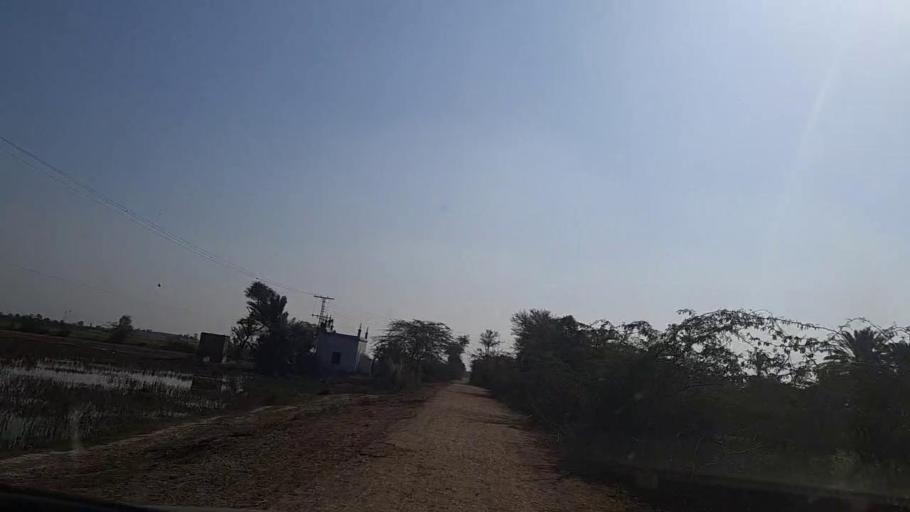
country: PK
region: Sindh
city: Sakrand
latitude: 26.0830
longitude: 68.3695
